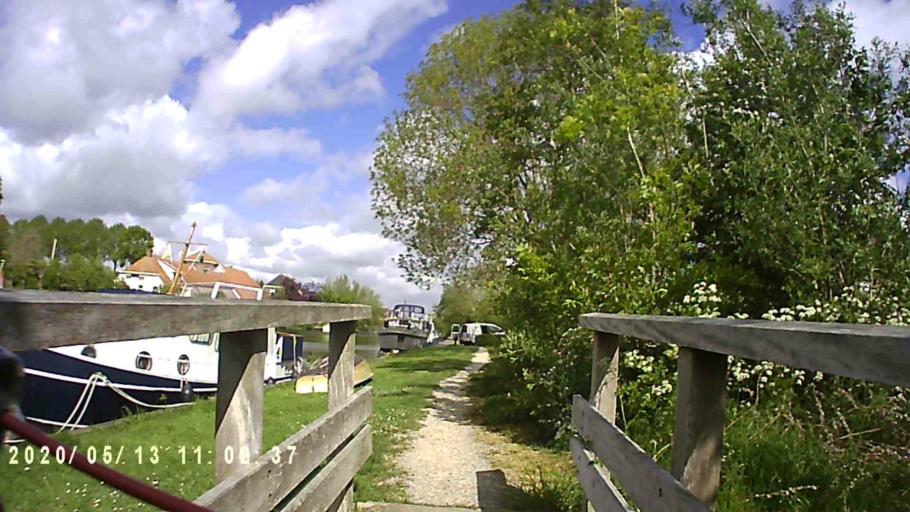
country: NL
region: Groningen
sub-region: Gemeente Zuidhorn
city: Grijpskerk
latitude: 53.2854
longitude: 6.3264
